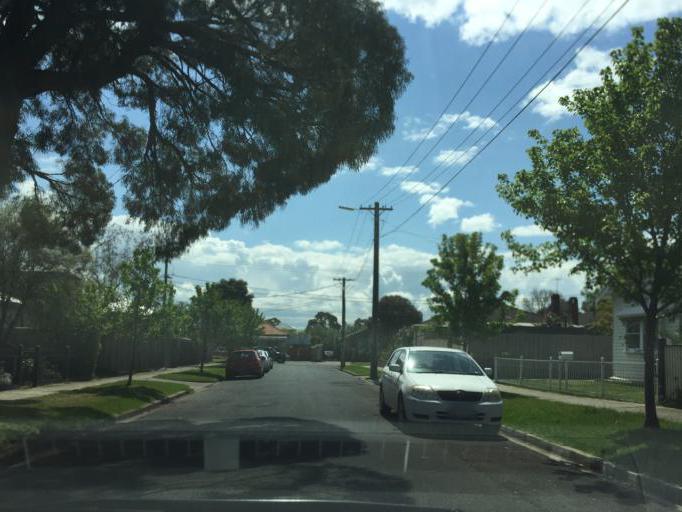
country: AU
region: Victoria
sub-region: Maribyrnong
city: West Footscray
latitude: -37.7912
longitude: 144.8735
